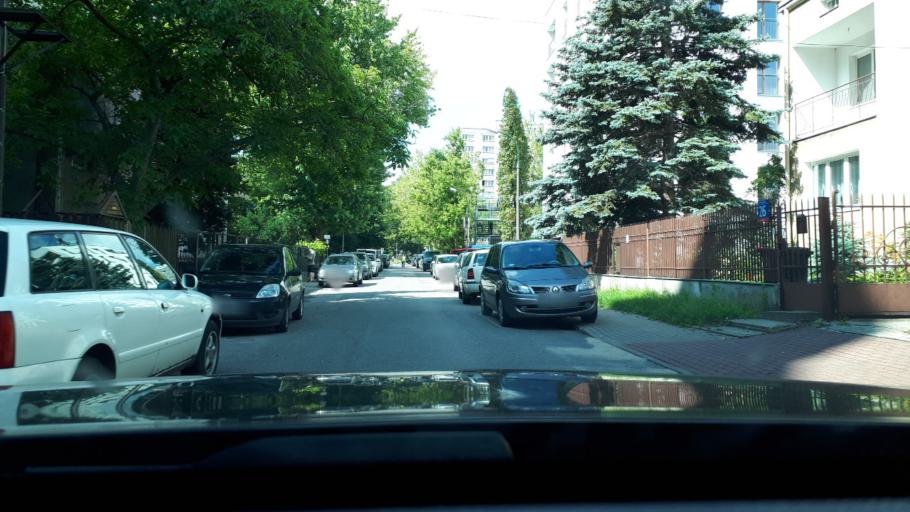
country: PL
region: Masovian Voivodeship
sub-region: Warszawa
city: Wilanow
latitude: 52.1762
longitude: 21.0678
